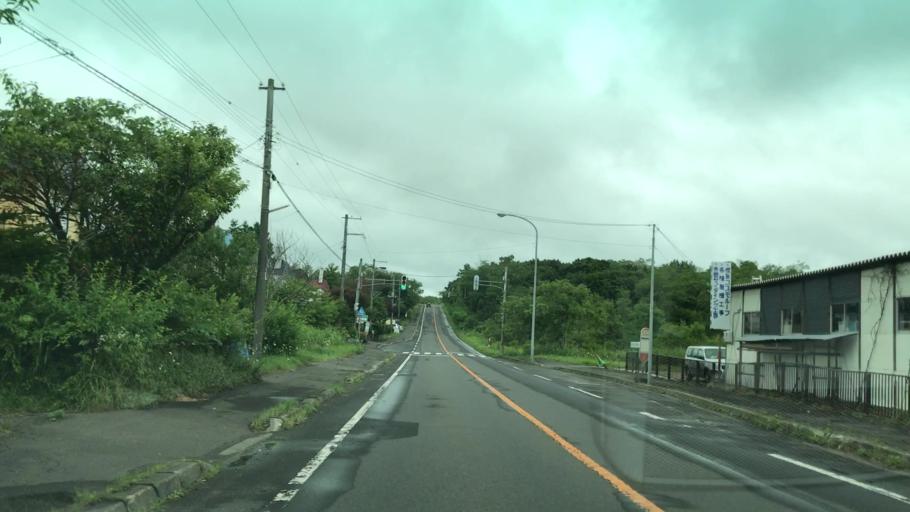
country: JP
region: Hokkaido
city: Muroran
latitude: 42.3819
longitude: 140.9774
